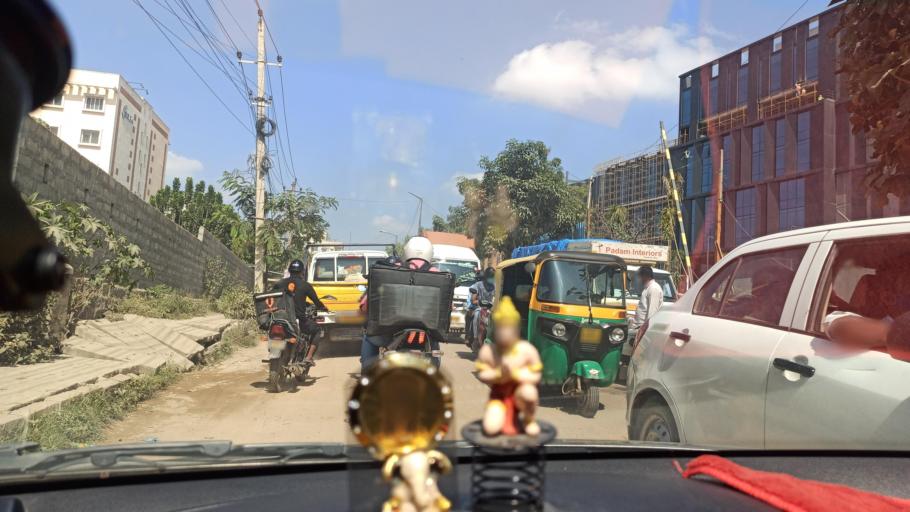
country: IN
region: Karnataka
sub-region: Bangalore Urban
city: Bangalore
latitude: 12.9699
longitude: 77.7069
